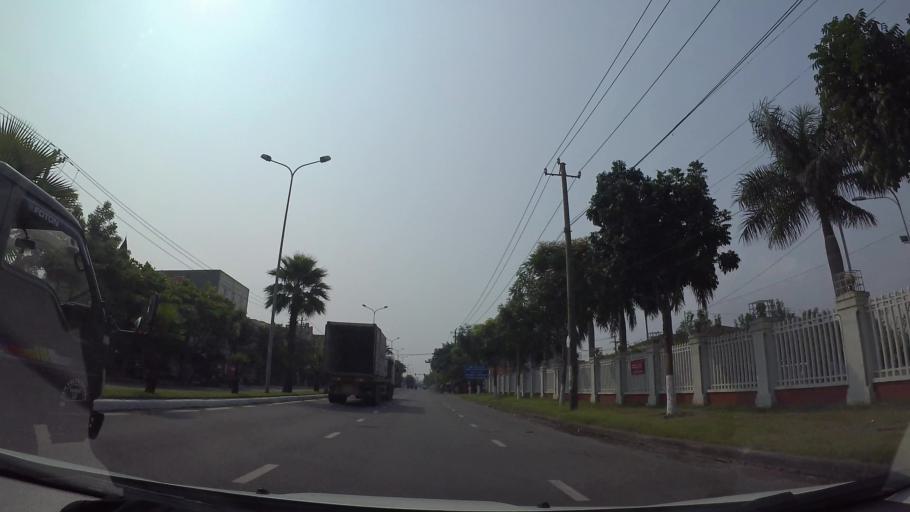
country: VN
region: Da Nang
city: Da Nang
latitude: 16.1073
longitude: 108.2461
